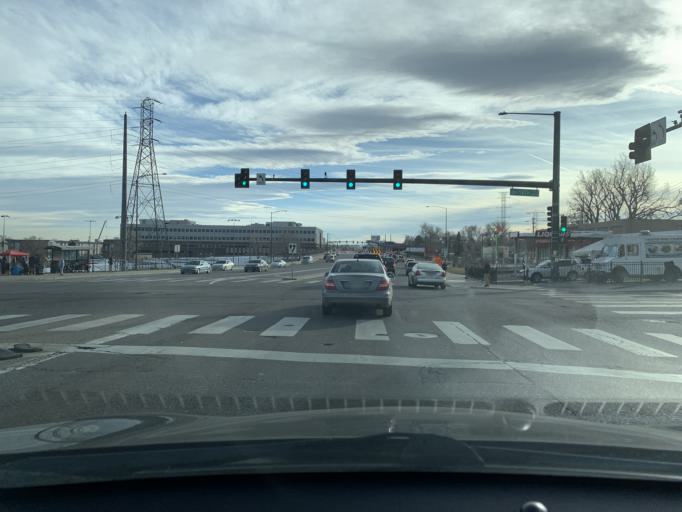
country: US
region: Colorado
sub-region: Denver County
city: Denver
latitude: 39.7382
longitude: -105.0253
